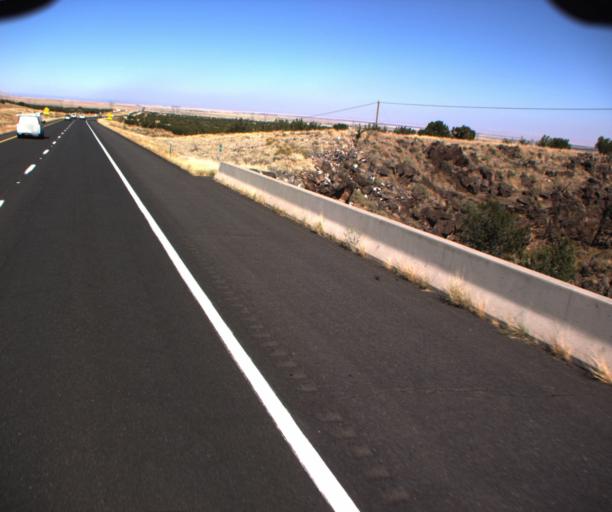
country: US
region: Arizona
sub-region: Coconino County
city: Flagstaff
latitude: 35.5181
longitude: -111.5438
